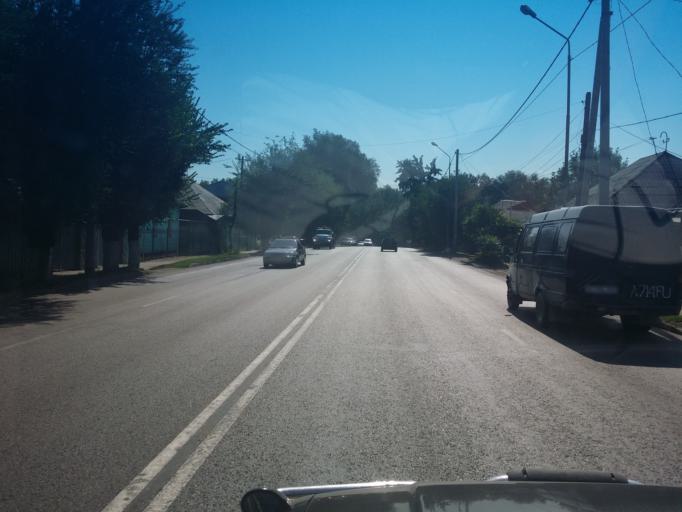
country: KZ
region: Almaty Oblysy
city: Pervomayskiy
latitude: 43.3510
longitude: 76.9608
